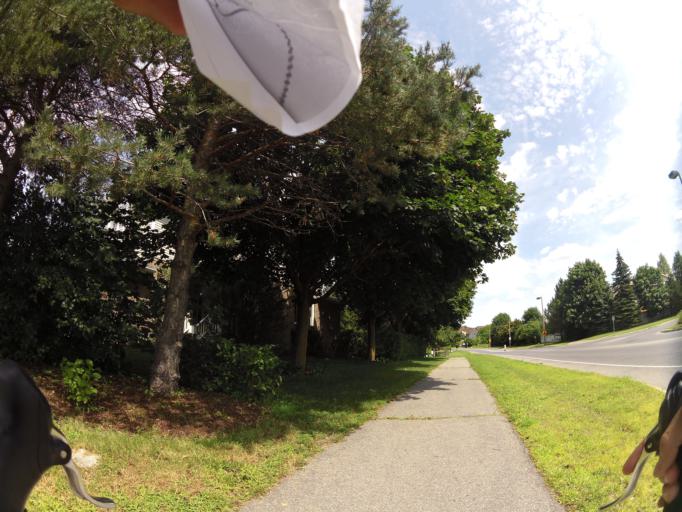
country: CA
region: Ontario
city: Bells Corners
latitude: 45.3521
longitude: -75.9257
